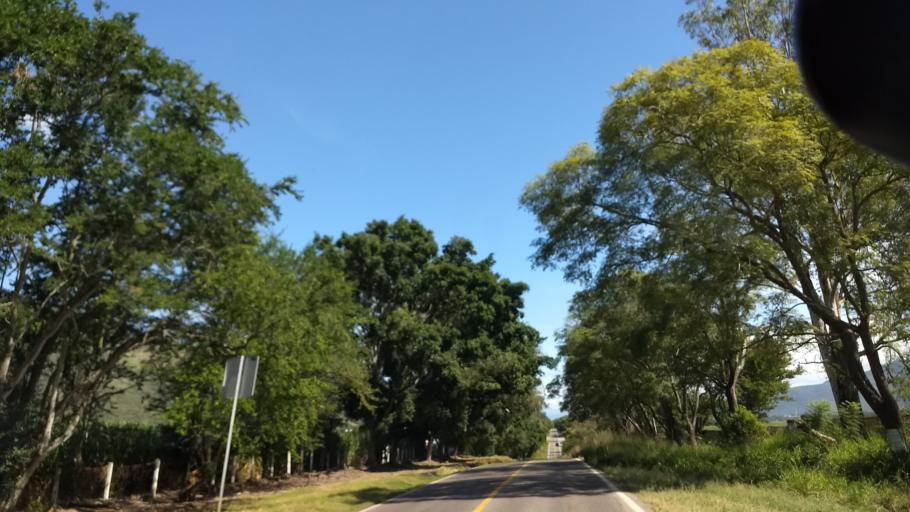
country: MX
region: Jalisco
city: Tuxpan
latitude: 19.5373
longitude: -103.4115
